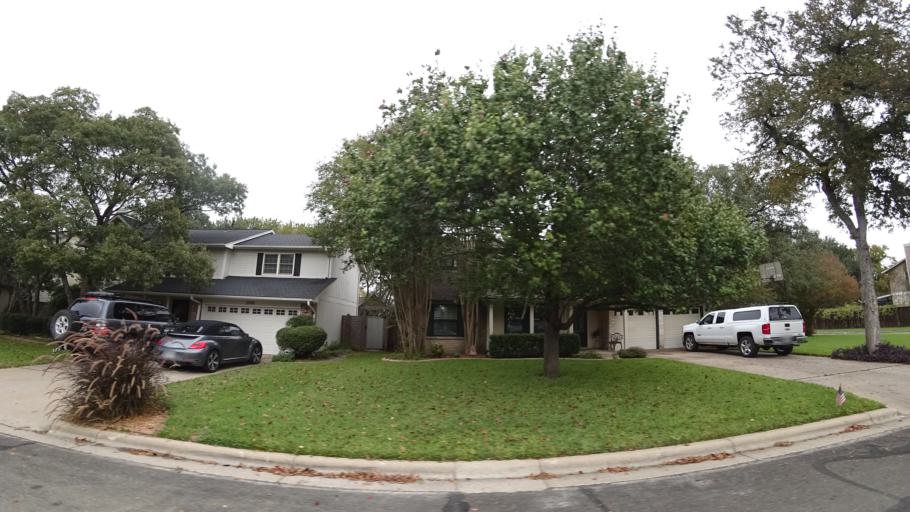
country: US
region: Texas
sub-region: Williamson County
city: Round Rock
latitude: 30.4833
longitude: -97.7043
